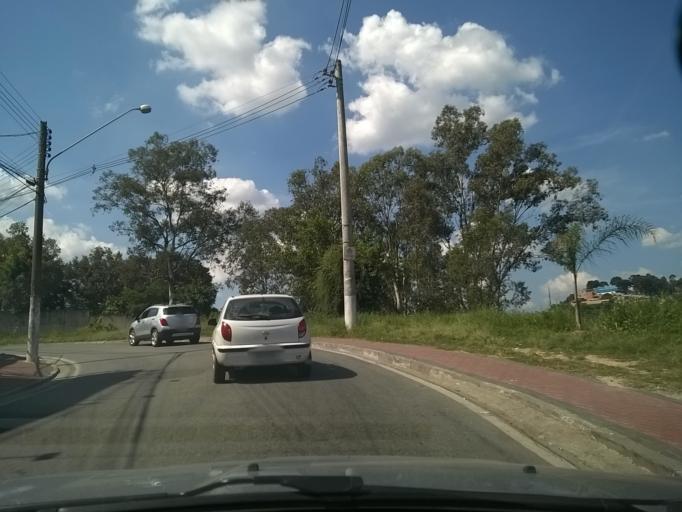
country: BR
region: Sao Paulo
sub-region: Francisco Morato
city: Francisco Morato
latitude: -23.2762
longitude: -46.7444
